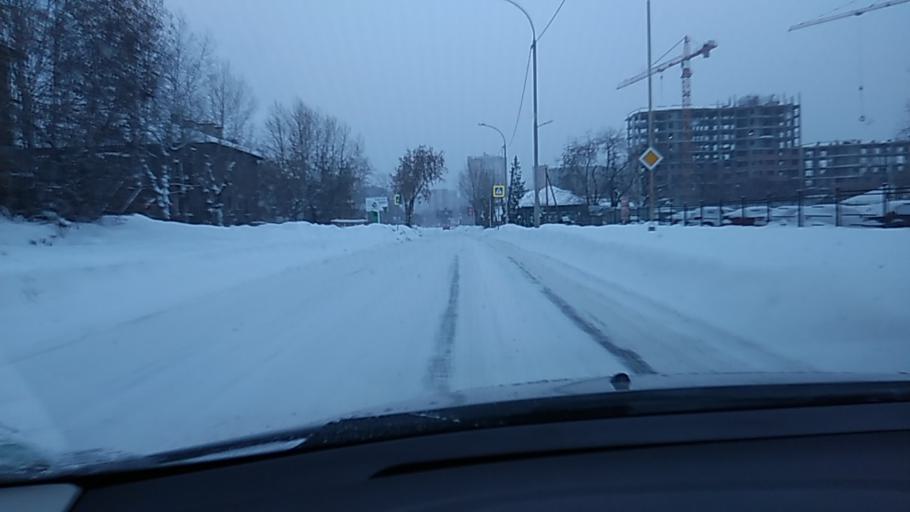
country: RU
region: Sverdlovsk
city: Sovkhoznyy
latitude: 56.8223
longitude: 60.5502
